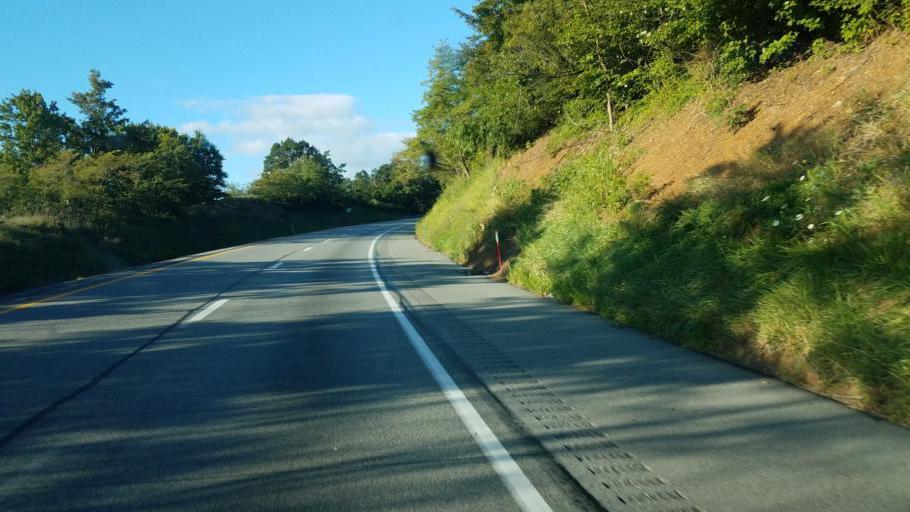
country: US
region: Pennsylvania
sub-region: Bedford County
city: Earlston
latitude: 39.8835
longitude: -78.2441
